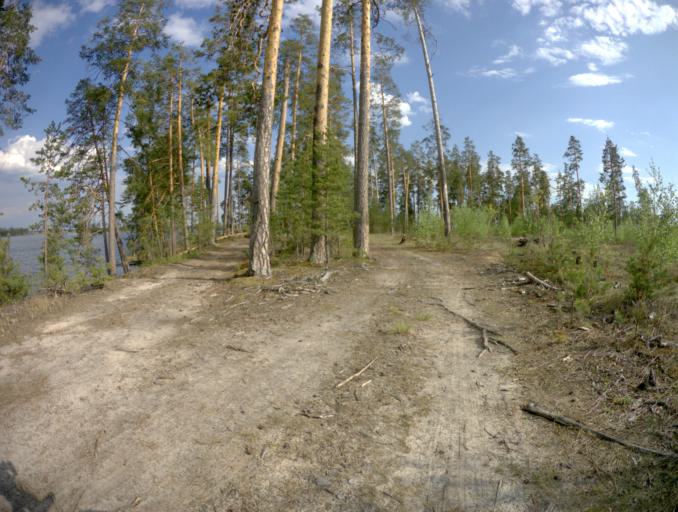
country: RU
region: Ivanovo
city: Talitsy
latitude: 56.4160
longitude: 42.2768
